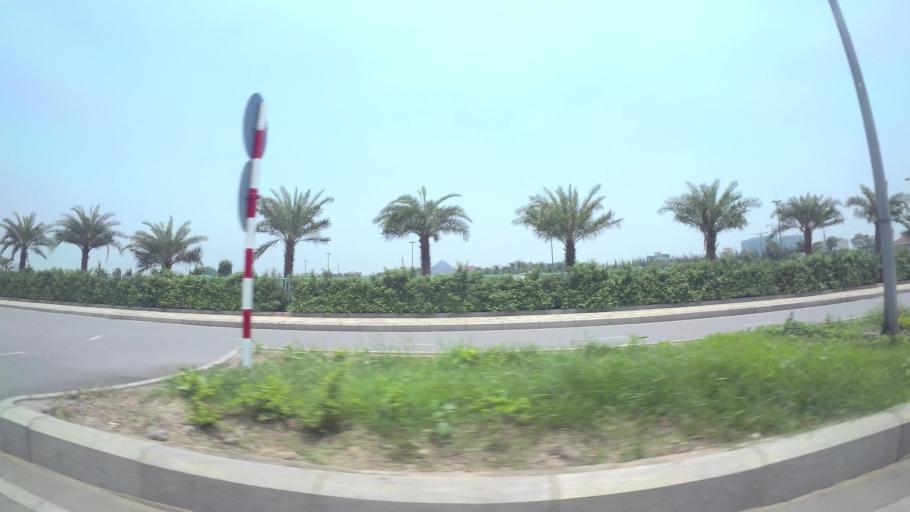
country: VN
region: Ha Noi
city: Trau Quy
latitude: 21.0387
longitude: 105.8954
